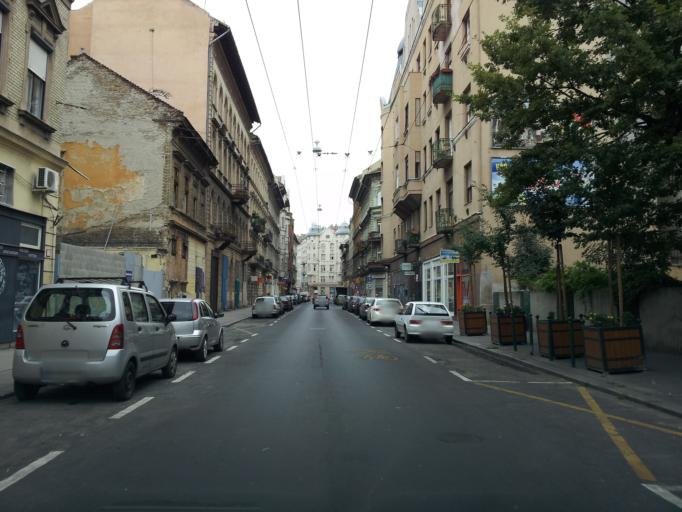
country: HU
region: Budapest
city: Budapest VII. keruelet
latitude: 47.5057
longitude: 19.0835
